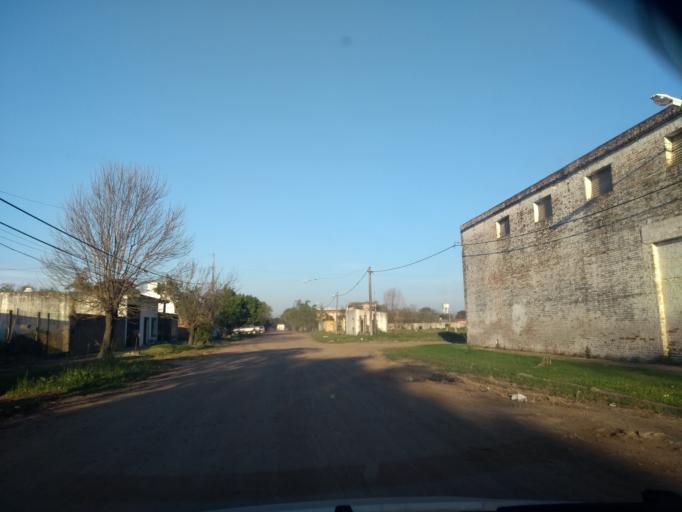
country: AR
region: Chaco
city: Barranqueras
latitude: -27.4759
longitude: -58.9597
